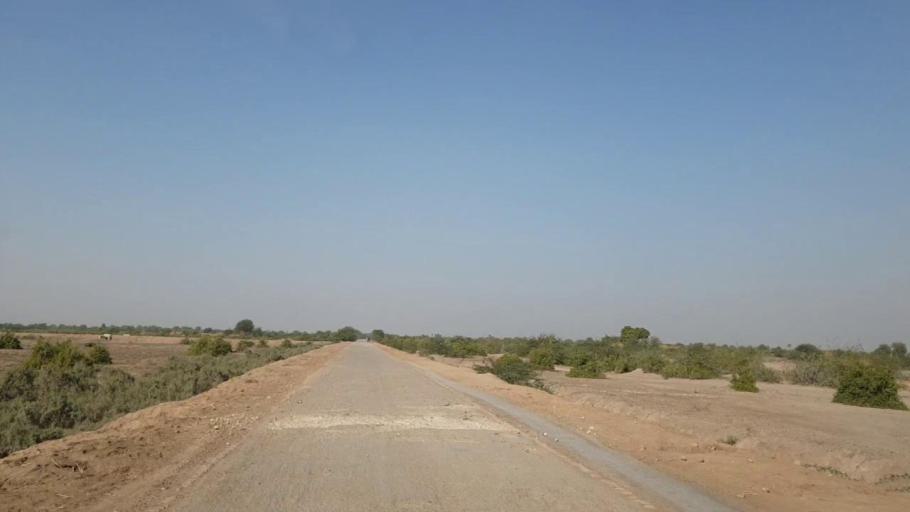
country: PK
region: Sindh
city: Digri
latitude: 24.9822
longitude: 69.1106
